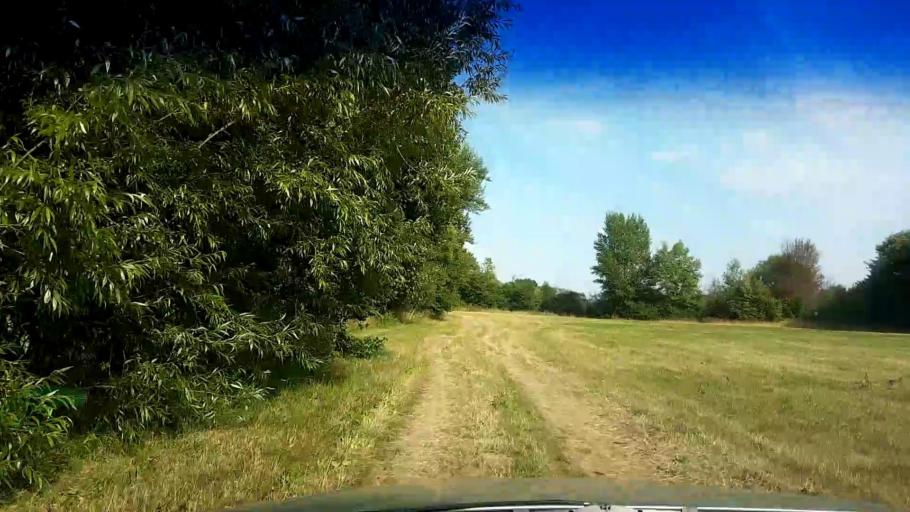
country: DE
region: Bavaria
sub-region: Regierungsbezirk Unterfranken
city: Stettfeld
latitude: 49.9673
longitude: 10.7050
